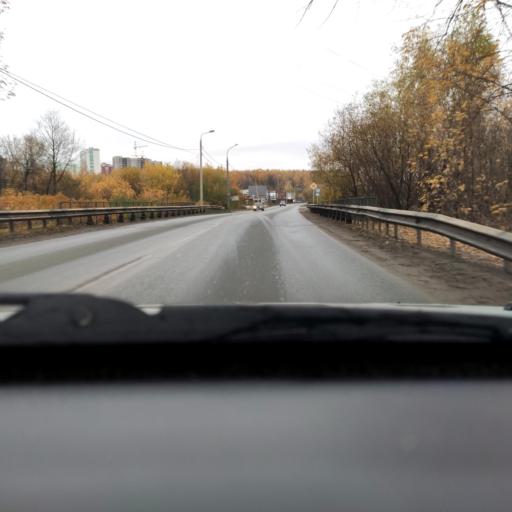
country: RU
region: Perm
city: Perm
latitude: 58.0762
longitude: 56.3496
